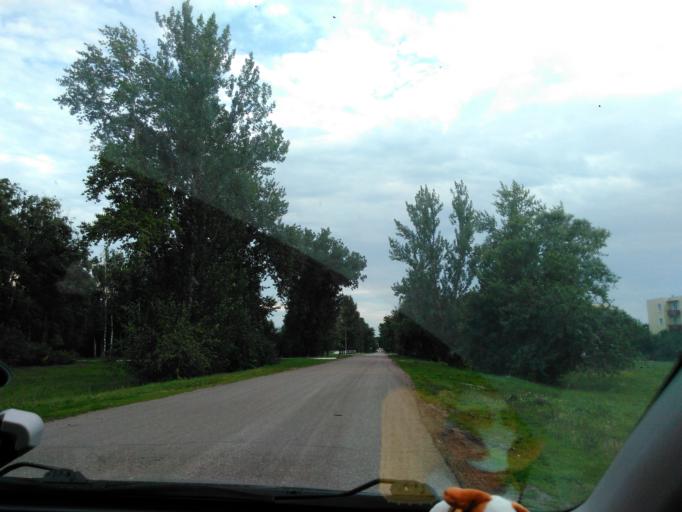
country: RU
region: Penza
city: Lermontovo
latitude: 52.9985
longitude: 43.6571
